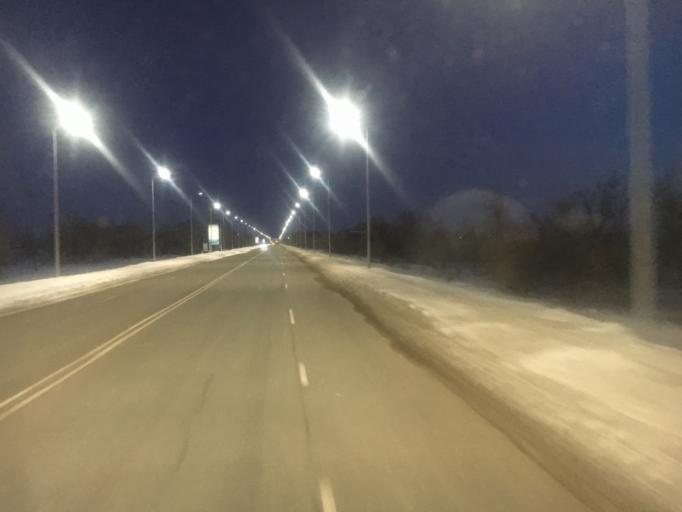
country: KZ
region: Batys Qazaqstan
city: Oral
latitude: 51.1617
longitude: 51.5283
